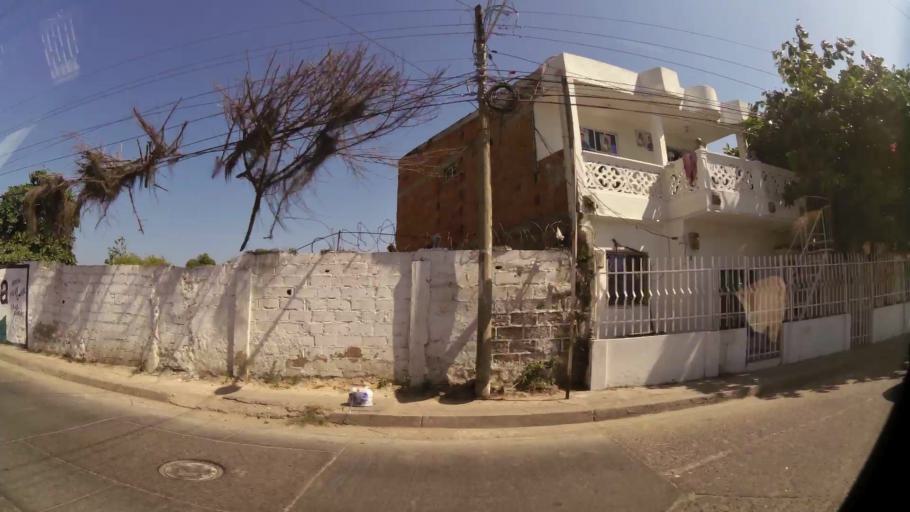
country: CO
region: Bolivar
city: Cartagena
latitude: 10.4150
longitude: -75.5201
